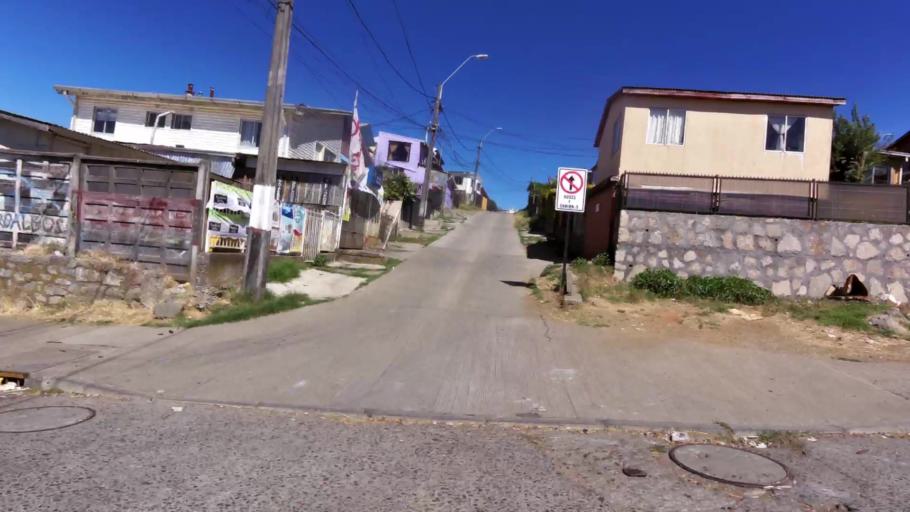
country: CL
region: Biobio
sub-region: Provincia de Concepcion
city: Penco
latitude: -36.7251
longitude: -72.9853
